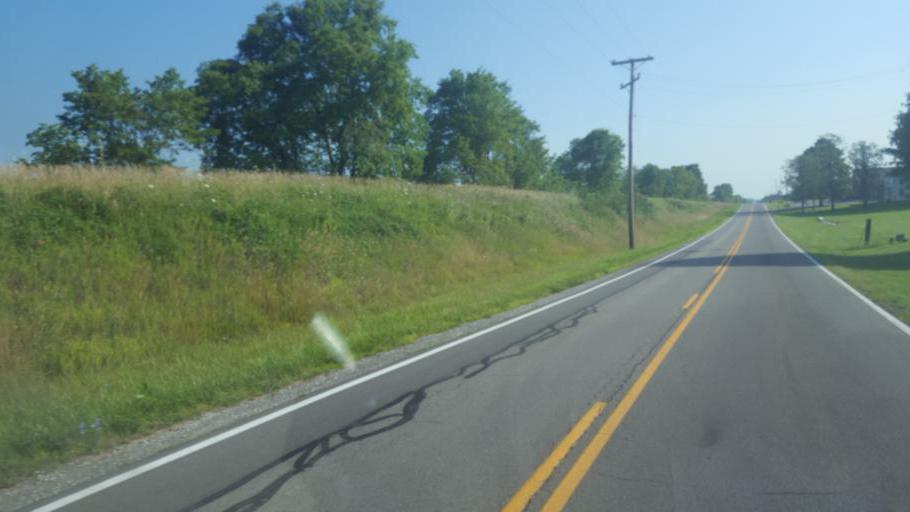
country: US
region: Ohio
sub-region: Hardin County
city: Kenton
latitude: 40.6643
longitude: -83.6038
